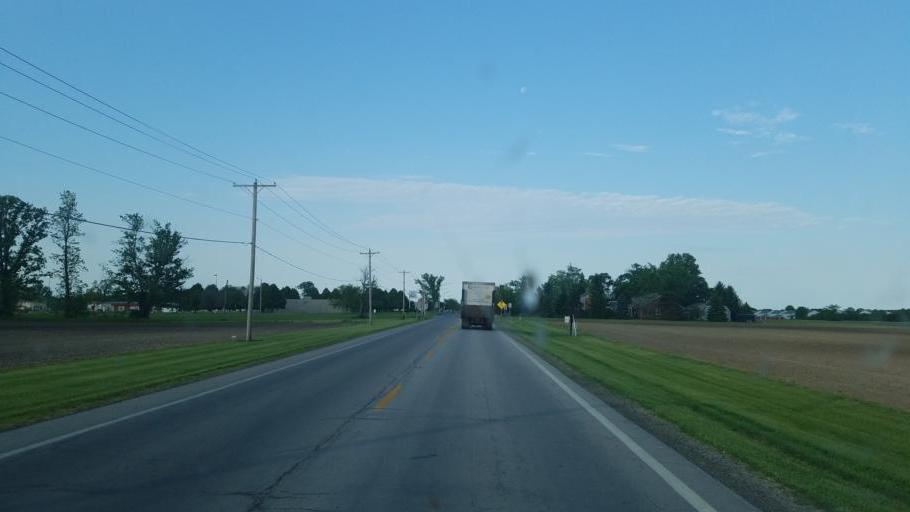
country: US
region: Ohio
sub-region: Fayette County
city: Washington Court House
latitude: 39.5559
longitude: -83.4174
